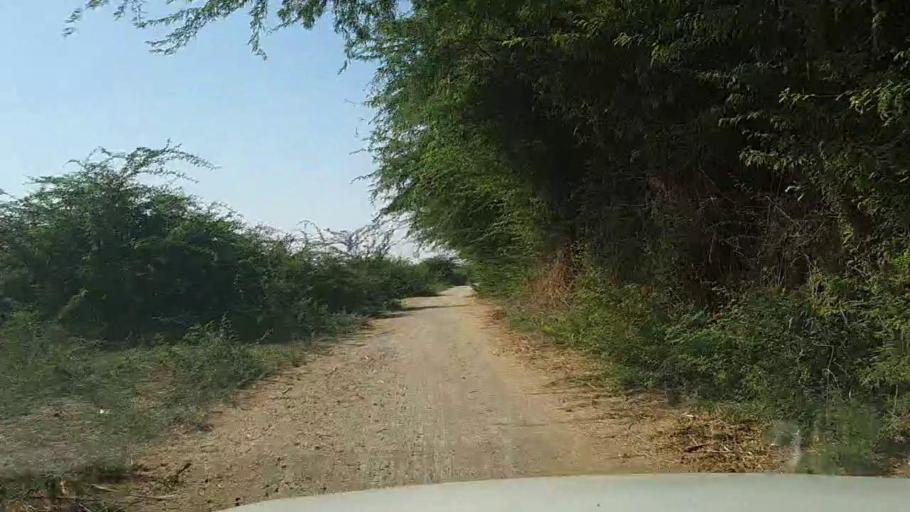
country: PK
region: Sindh
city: Mirpur Batoro
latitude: 24.6935
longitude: 68.1695
